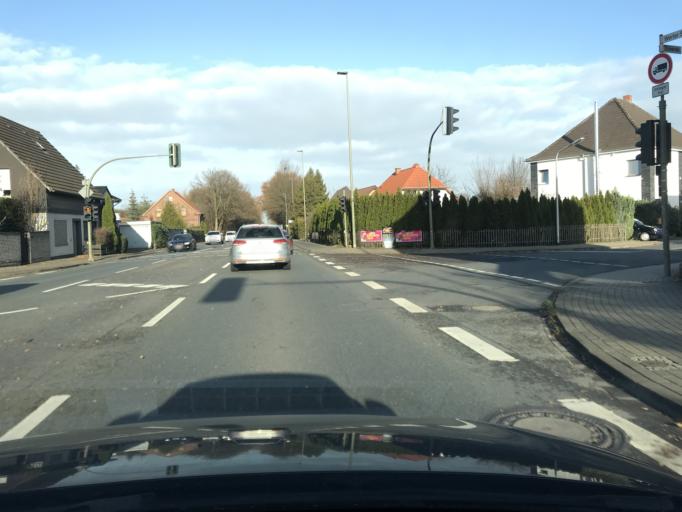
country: DE
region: North Rhine-Westphalia
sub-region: Regierungsbezirk Arnsberg
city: Hamm
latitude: 51.6494
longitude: 7.8412
